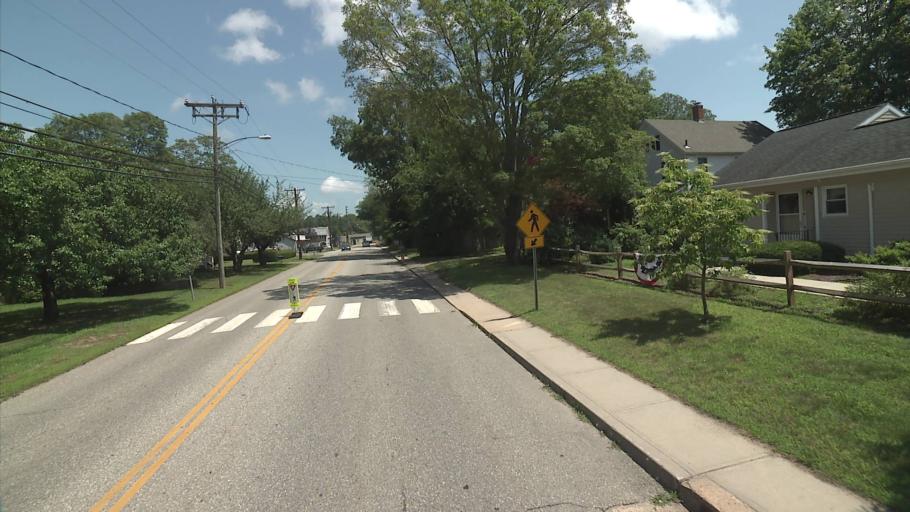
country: US
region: Connecticut
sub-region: Middlesex County
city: Essex Village
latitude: 41.3519
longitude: -72.4086
